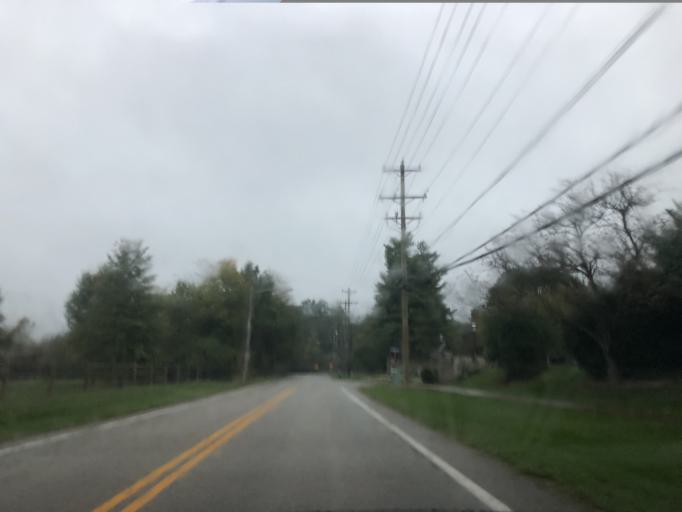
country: US
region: Ohio
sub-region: Hamilton County
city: The Village of Indian Hill
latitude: 39.2457
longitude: -84.3104
